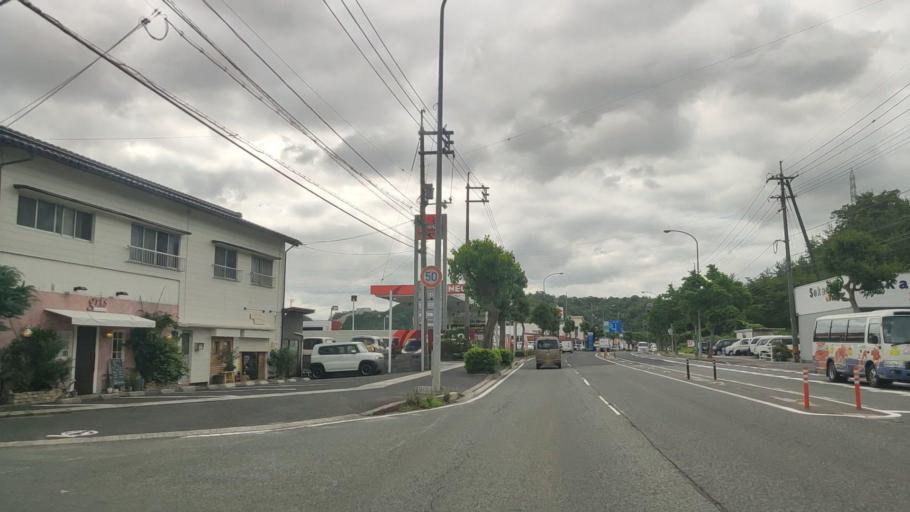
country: JP
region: Tottori
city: Yonago
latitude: 35.4207
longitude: 133.3500
